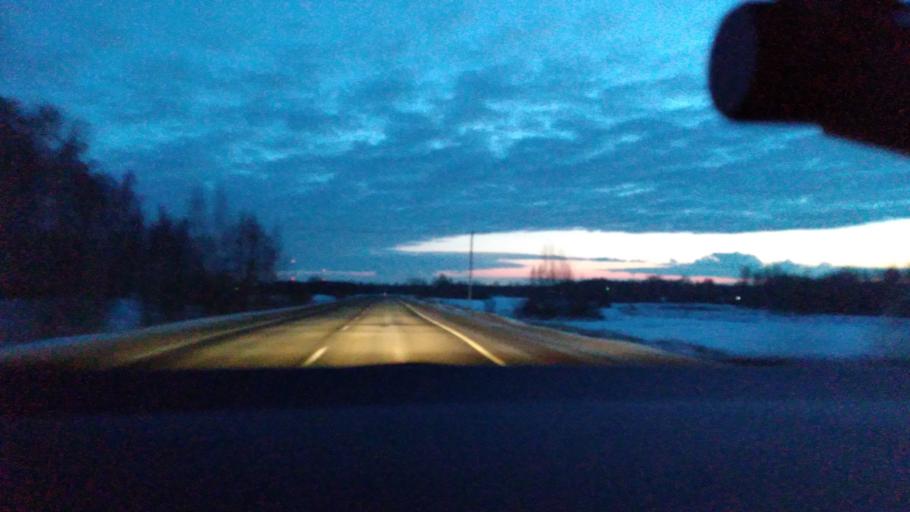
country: RU
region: Moskovskaya
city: Krasnaya Poyma
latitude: 55.1482
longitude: 39.2174
